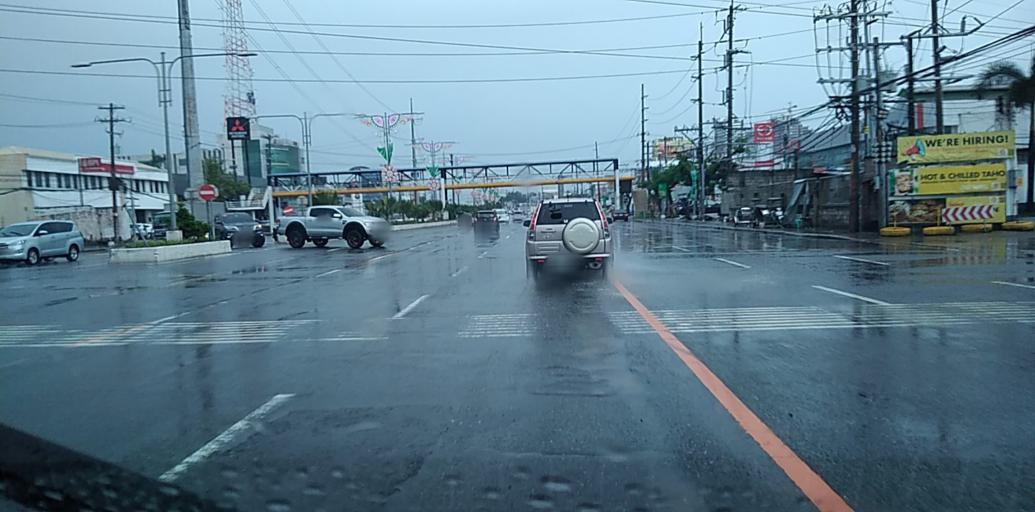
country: PH
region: Central Luzon
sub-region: Province of Pampanga
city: Del Pilar
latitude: 15.0442
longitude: 120.6883
